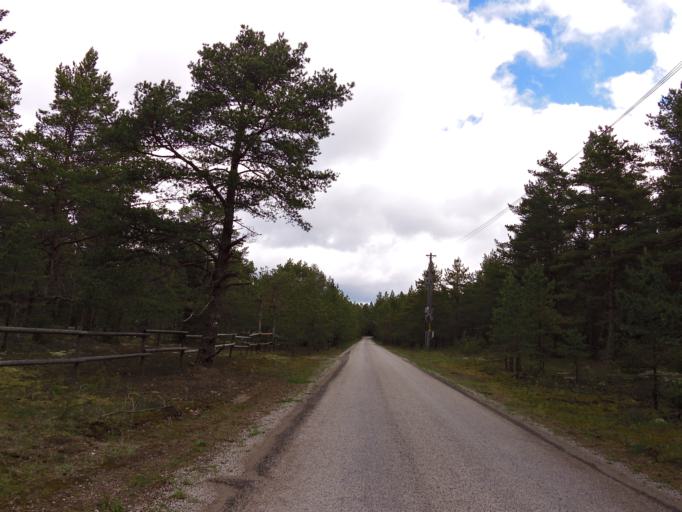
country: EE
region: Harju
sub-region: Paldiski linn
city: Paldiski
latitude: 59.2711
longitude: 23.7779
